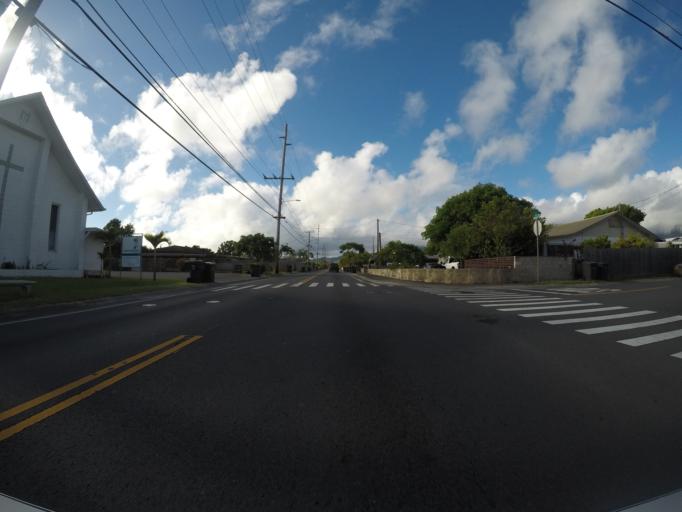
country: US
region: Hawaii
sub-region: Honolulu County
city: Kailua
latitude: 21.4025
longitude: -157.7493
